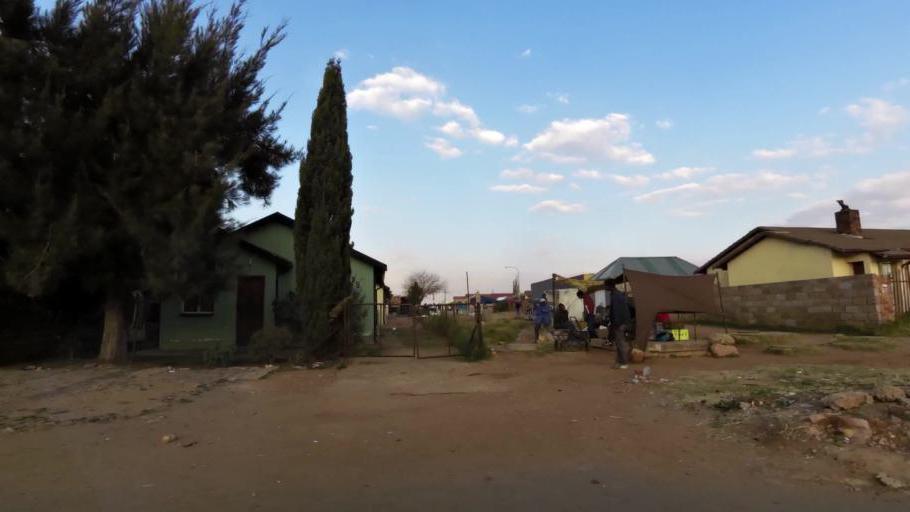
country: ZA
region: Gauteng
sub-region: City of Johannesburg Metropolitan Municipality
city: Roodepoort
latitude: -26.2099
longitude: 27.8955
